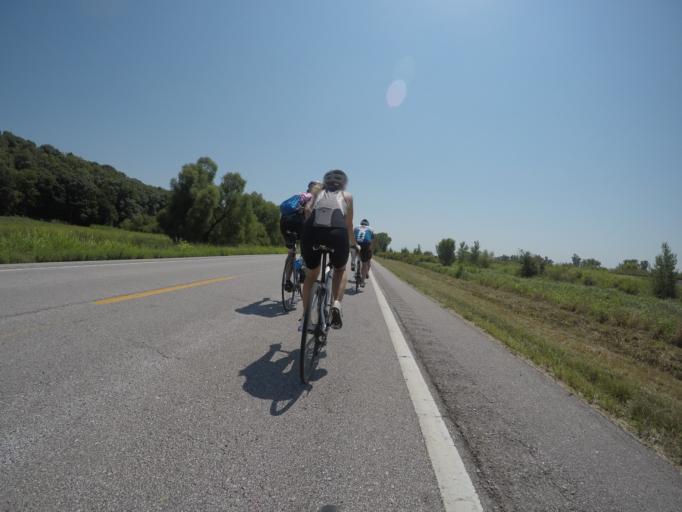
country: US
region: Kansas
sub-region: Leavenworth County
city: Leavenworth
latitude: 39.3418
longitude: -94.8624
